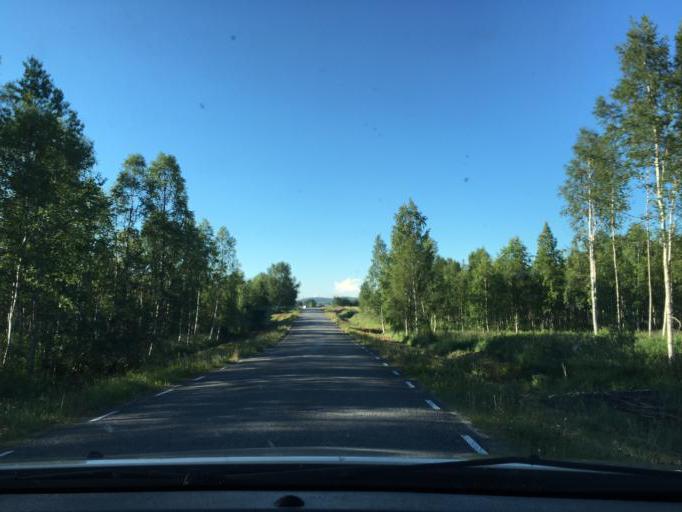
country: SE
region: Norrbotten
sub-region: Kalix Kommun
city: Toere
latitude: 66.0979
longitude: 22.7792
